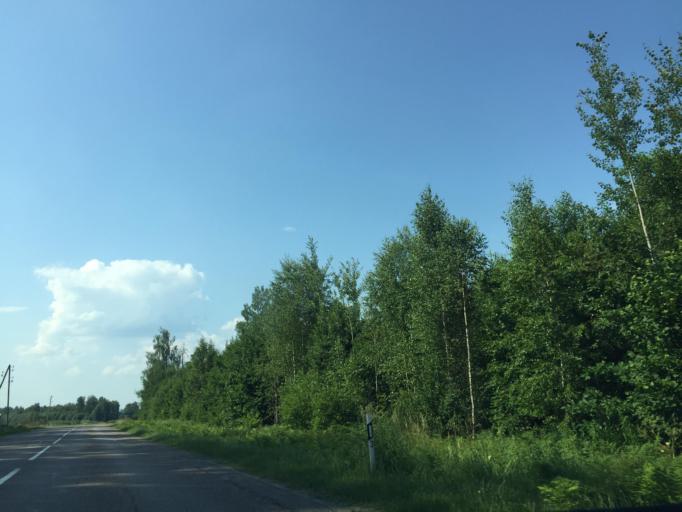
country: LV
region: Limbazu Rajons
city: Limbazi
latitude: 57.4920
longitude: 24.8498
